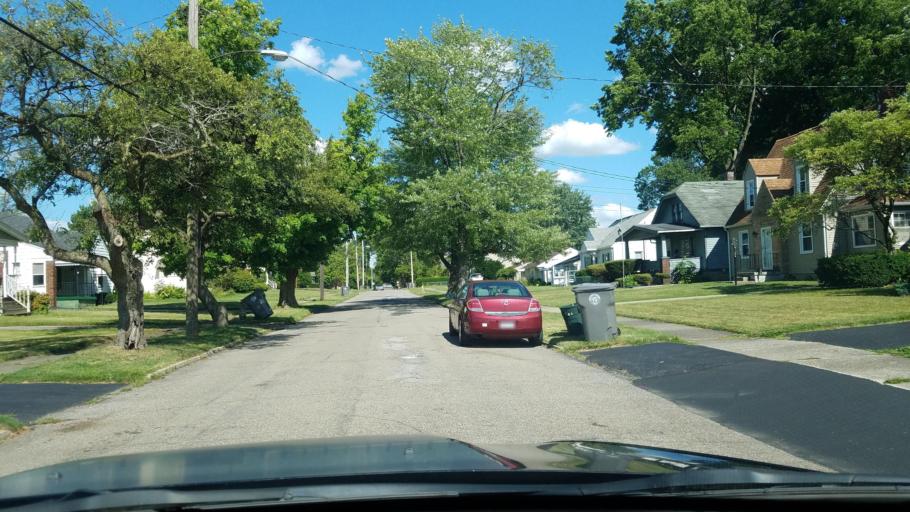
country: US
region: Ohio
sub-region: Mahoning County
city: Struthers
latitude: 41.0596
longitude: -80.6240
